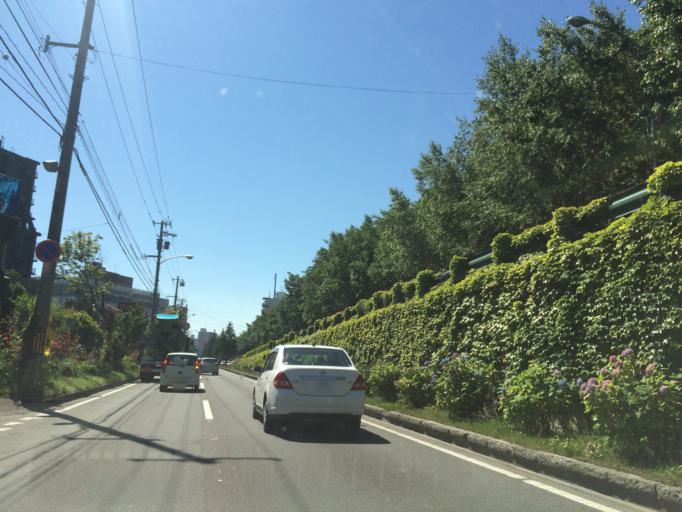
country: JP
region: Hokkaido
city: Sapporo
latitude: 43.0508
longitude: 141.3175
